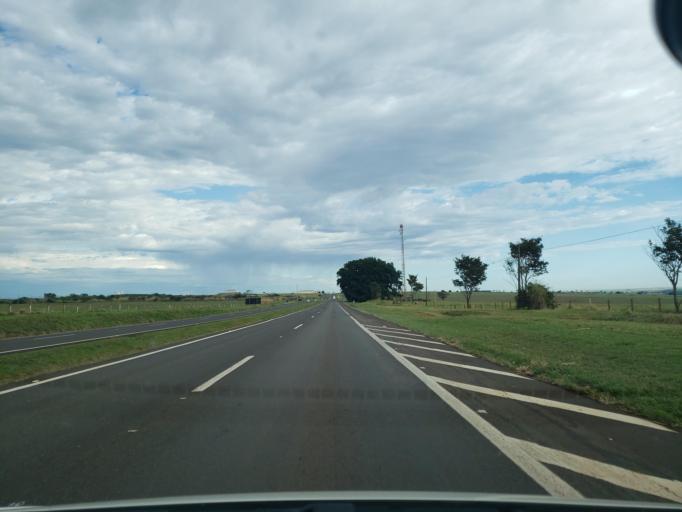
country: BR
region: Sao Paulo
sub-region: Jau
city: Jau
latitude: -22.2683
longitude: -48.4941
